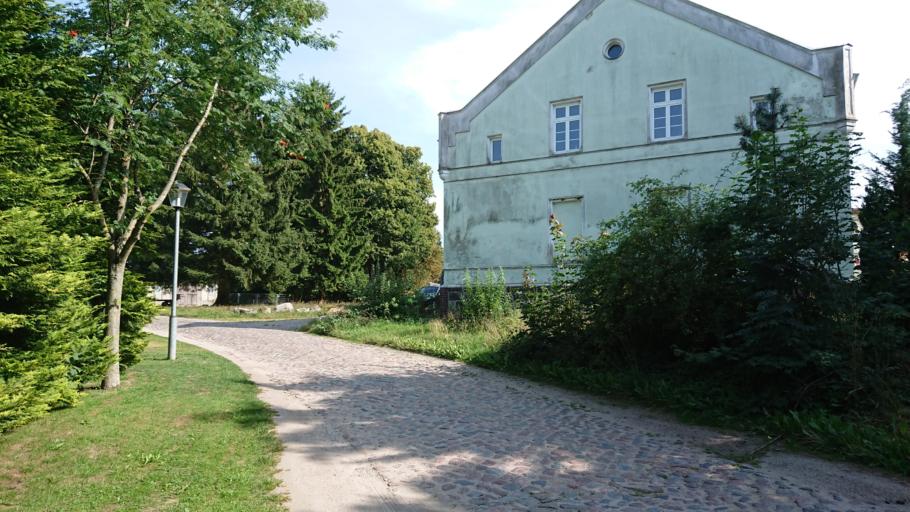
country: DE
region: Mecklenburg-Vorpommern
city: Gormin
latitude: 53.9824
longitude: 13.2813
